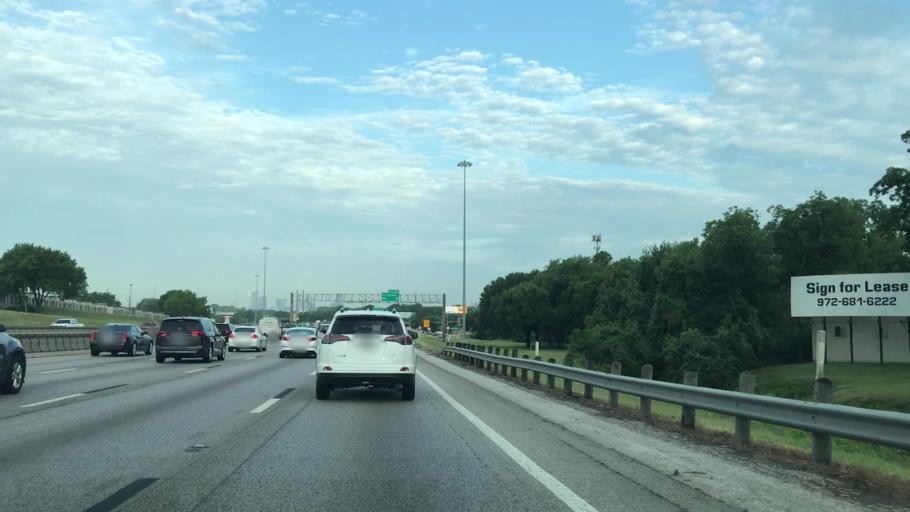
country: US
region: Texas
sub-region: Dallas County
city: Highland Park
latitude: 32.7951
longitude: -96.7173
